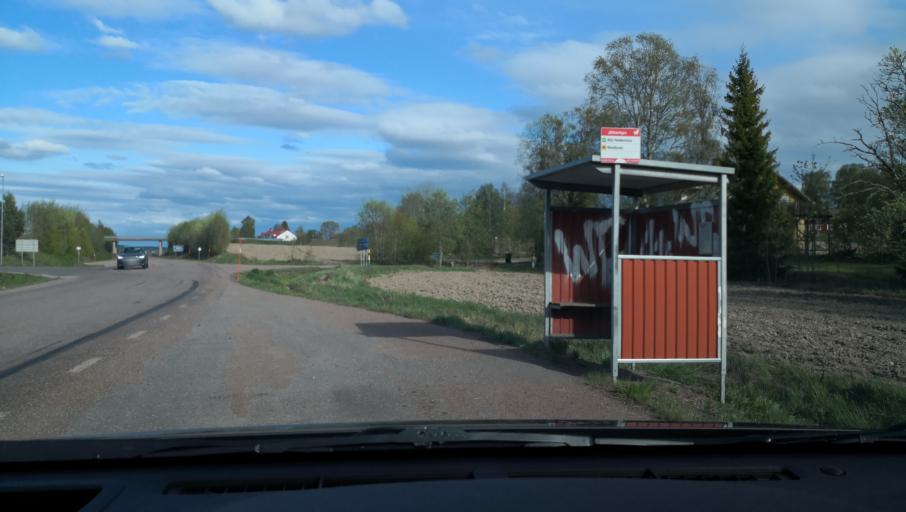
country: SE
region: Dalarna
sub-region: Saters Kommun
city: Saeter
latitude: 60.2974
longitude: 15.8605
